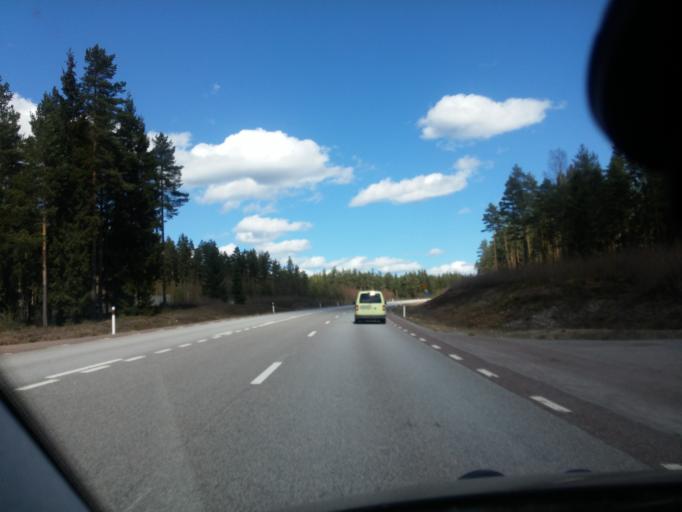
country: SE
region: Dalarna
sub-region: Faluns Kommun
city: Falun
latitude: 60.6704
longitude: 15.6473
